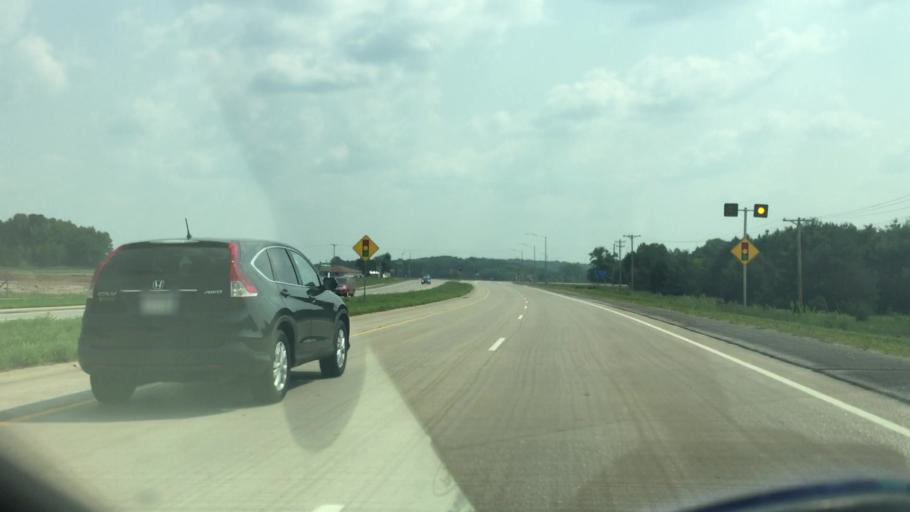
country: US
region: Wisconsin
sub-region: Eau Claire County
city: Altoona
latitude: 44.7443
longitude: -91.4505
